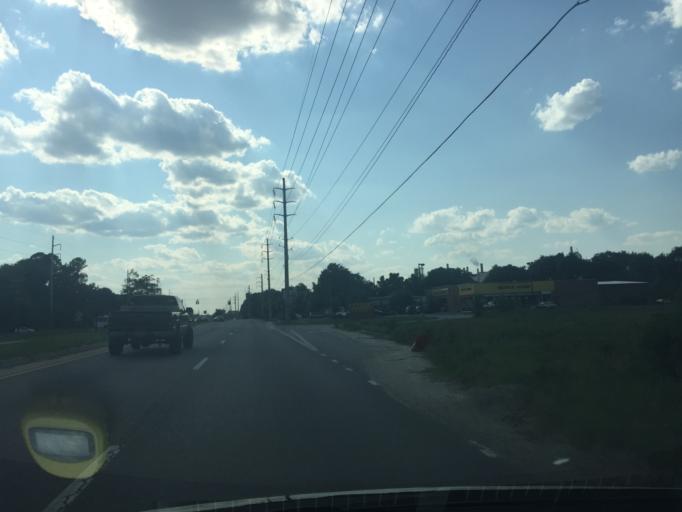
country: US
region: Georgia
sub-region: Chatham County
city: Thunderbolt
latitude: 32.0695
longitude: -81.0554
